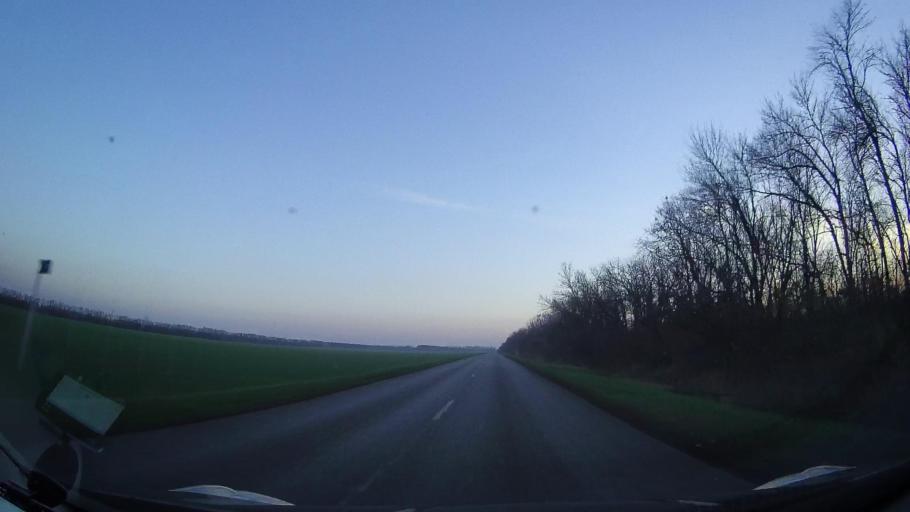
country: RU
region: Rostov
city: Zernograd
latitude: 46.9813
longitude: 40.3915
